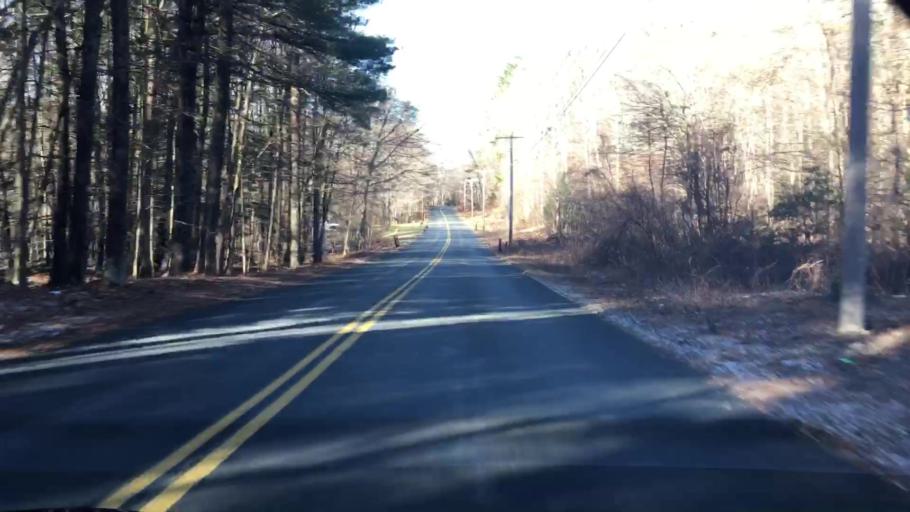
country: US
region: Connecticut
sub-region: Tolland County
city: Somers
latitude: 41.9636
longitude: -72.4095
